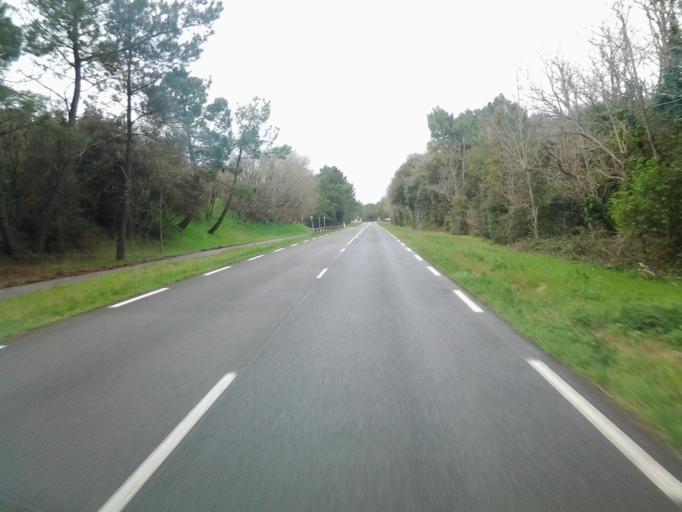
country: FR
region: Pays de la Loire
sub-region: Departement de la Vendee
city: La Tranche-sur-Mer
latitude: 46.3704
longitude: -1.4601
